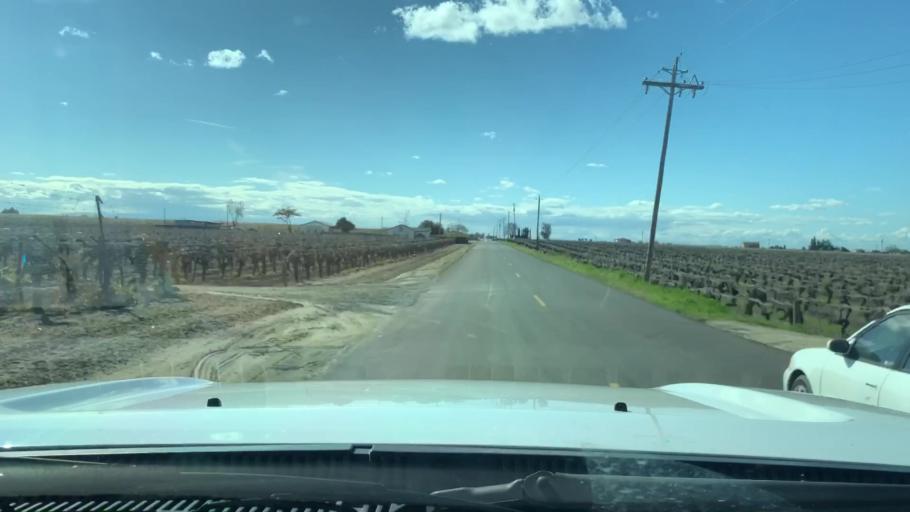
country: US
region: California
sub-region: Fresno County
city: Caruthers
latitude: 36.5619
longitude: -119.7751
